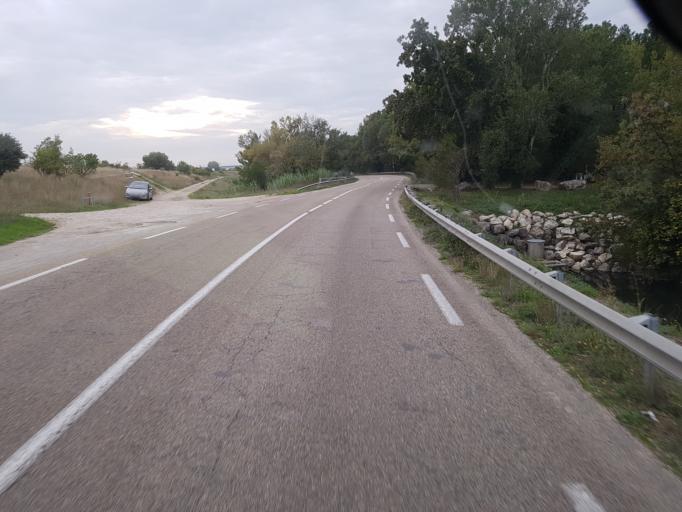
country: FR
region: Languedoc-Roussillon
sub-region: Departement du Gard
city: Les Angles
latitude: 43.9420
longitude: 4.7789
